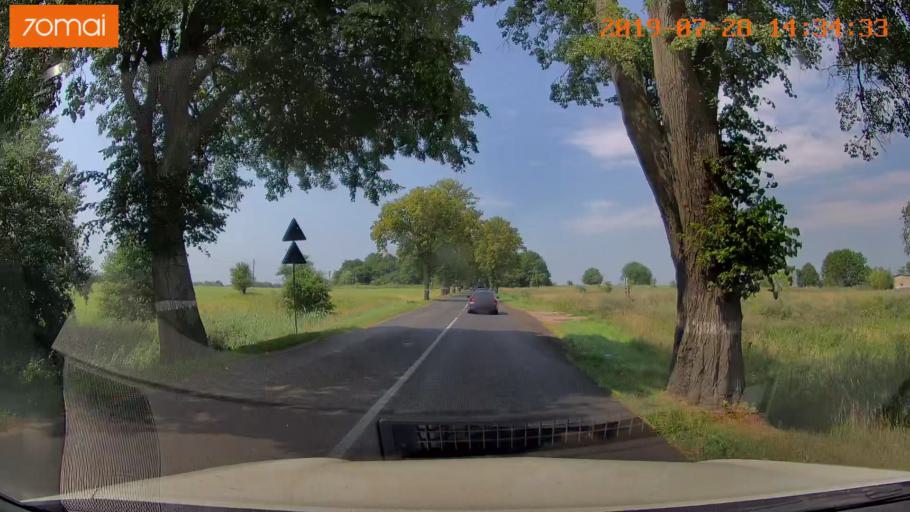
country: RU
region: Kaliningrad
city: Primorsk
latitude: 54.8259
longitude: 20.0171
